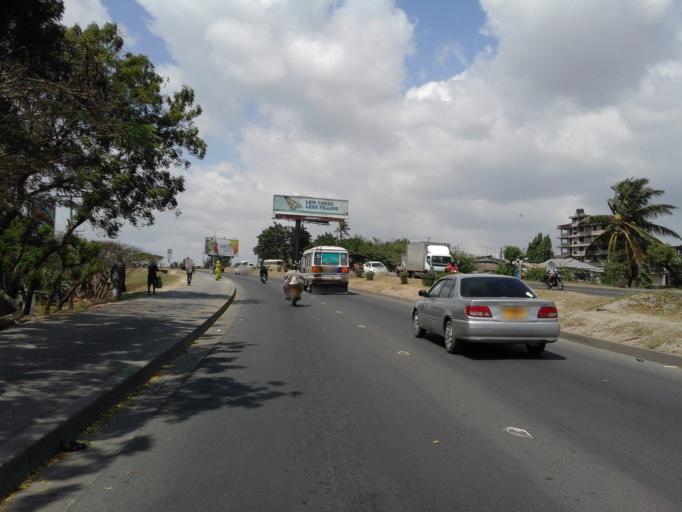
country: TZ
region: Dar es Salaam
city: Magomeni
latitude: -6.8146
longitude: 39.2543
